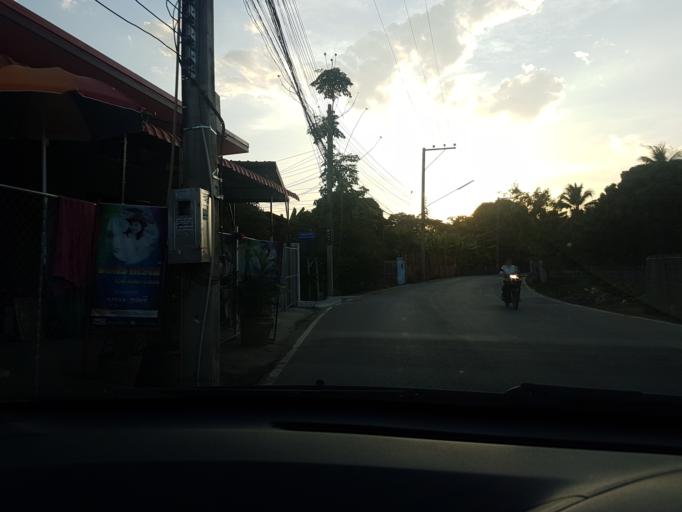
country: TH
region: Chiang Mai
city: San Sai
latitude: 18.8354
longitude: 99.0452
